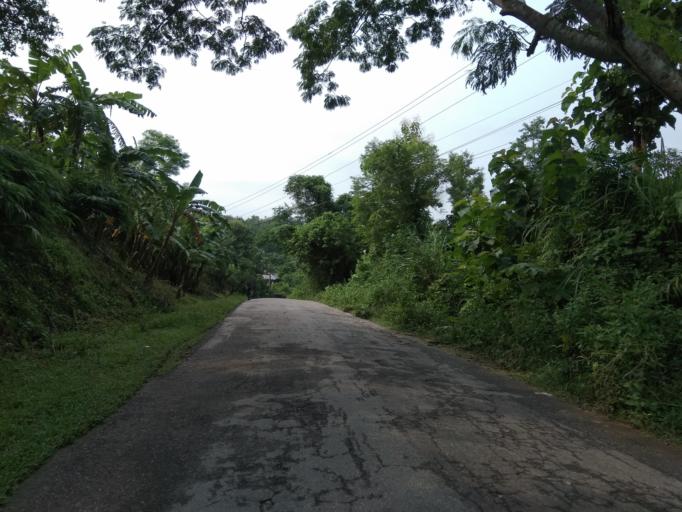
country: BD
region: Chittagong
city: Khagrachhari
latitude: 23.0081
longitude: 92.0107
